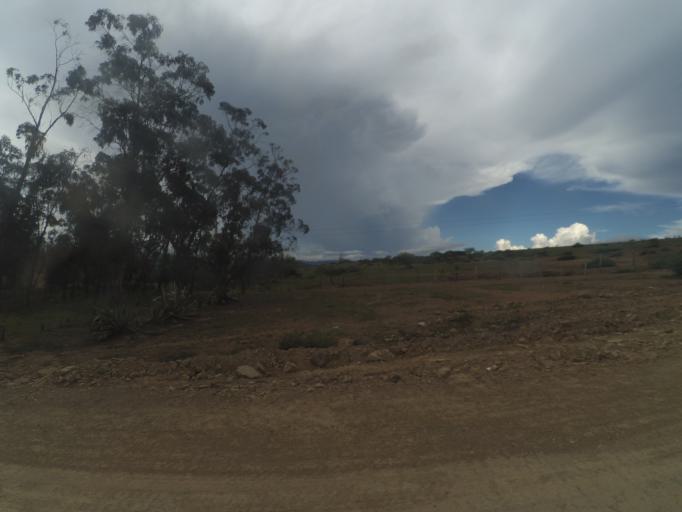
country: BO
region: Chuquisaca
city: Padilla
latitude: -19.3447
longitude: -64.2939
